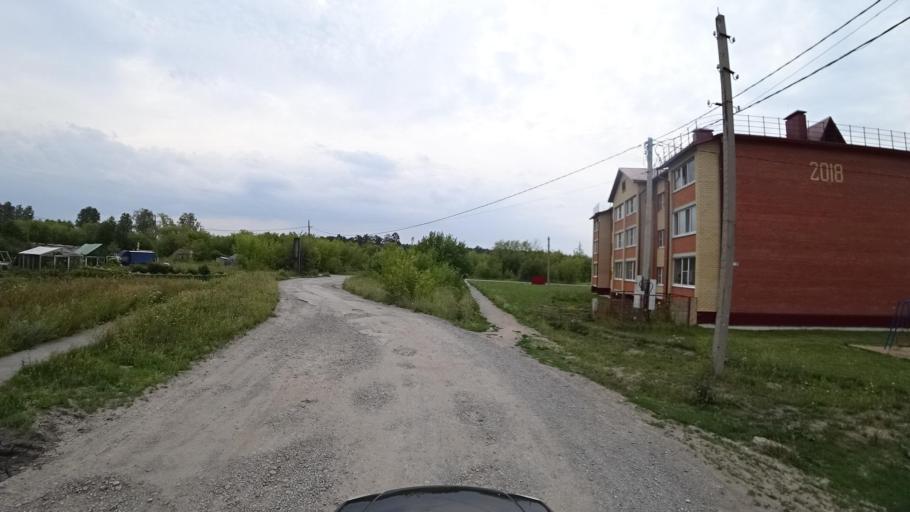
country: RU
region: Sverdlovsk
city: Kamyshlov
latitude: 56.8453
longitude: 62.7430
